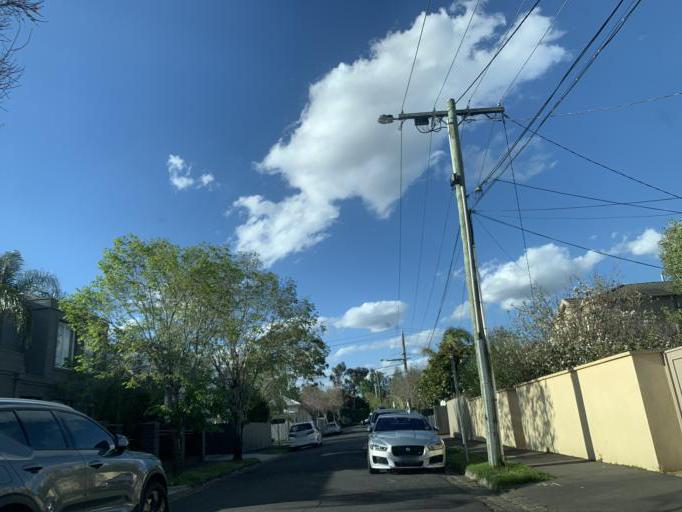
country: AU
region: Victoria
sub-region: Bayside
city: North Brighton
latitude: -37.9033
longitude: 144.9996
